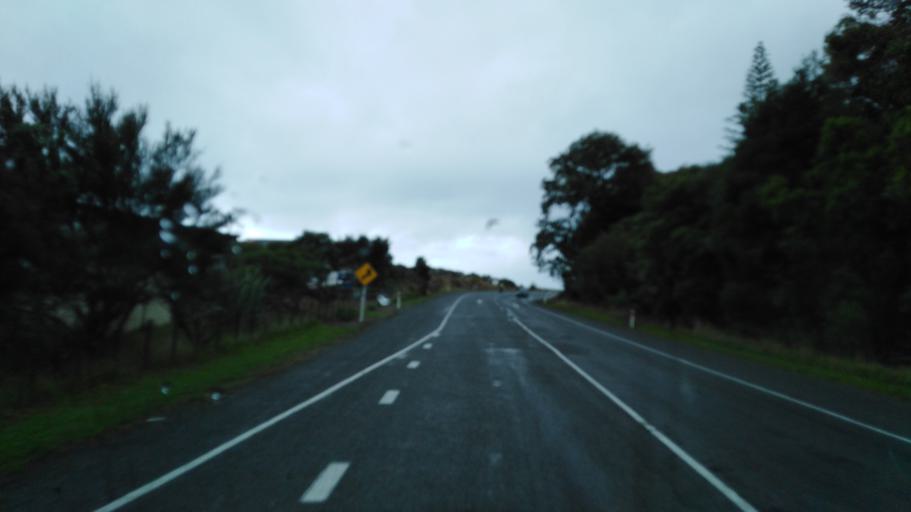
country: NZ
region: Nelson
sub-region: Nelson City
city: Nelson
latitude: -41.2168
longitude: 173.3301
